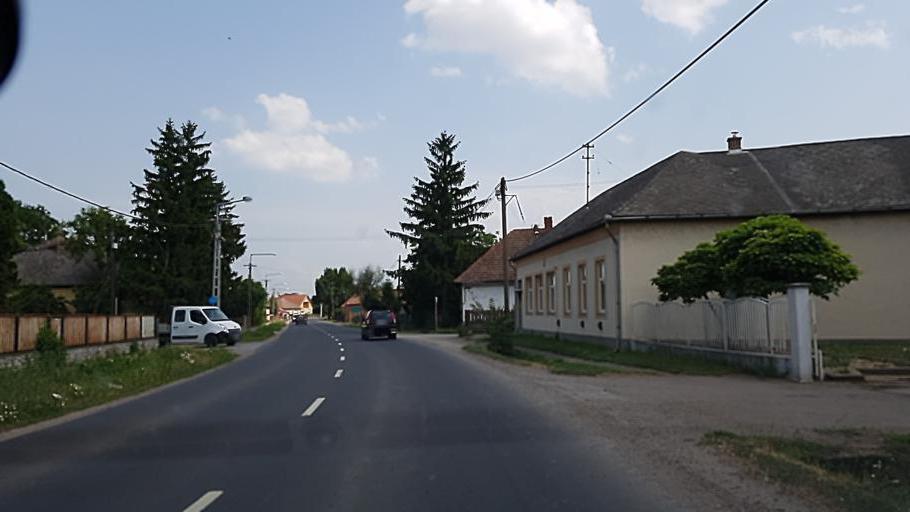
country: HU
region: Heves
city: Besenyotelek
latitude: 47.6975
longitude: 20.4293
